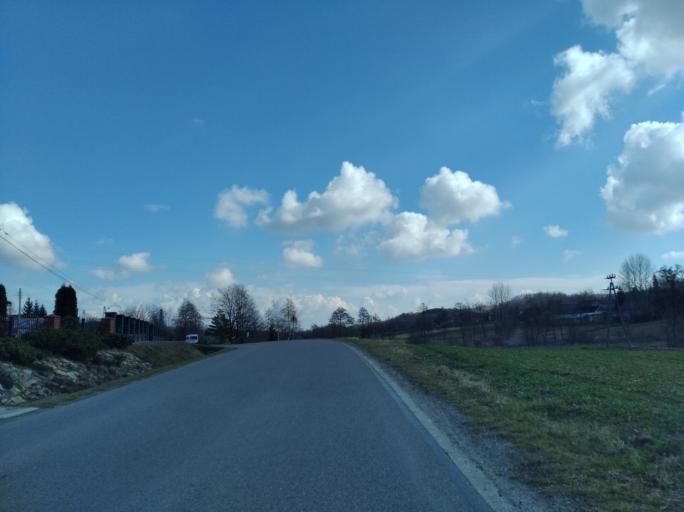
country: PL
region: Subcarpathian Voivodeship
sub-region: Powiat debicki
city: Brzostek
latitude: 49.8603
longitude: 21.4704
